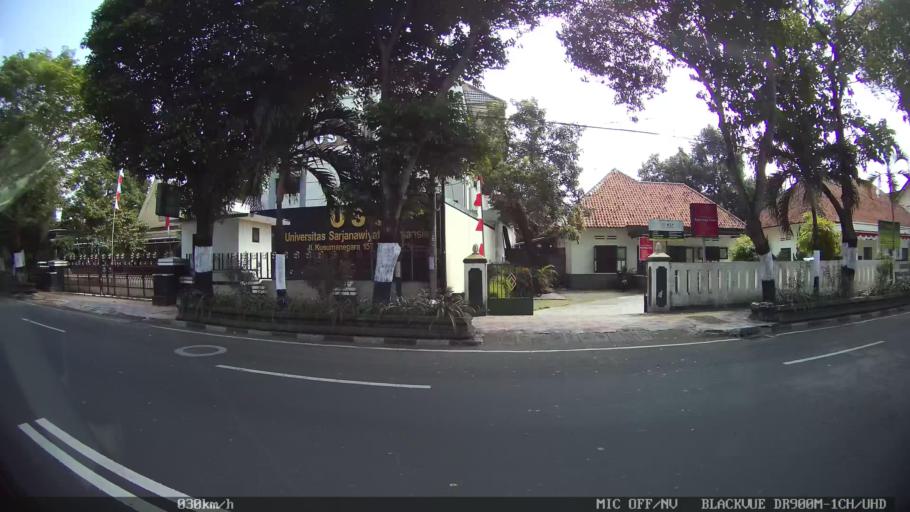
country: ID
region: Daerah Istimewa Yogyakarta
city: Yogyakarta
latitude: -7.8022
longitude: 110.3926
